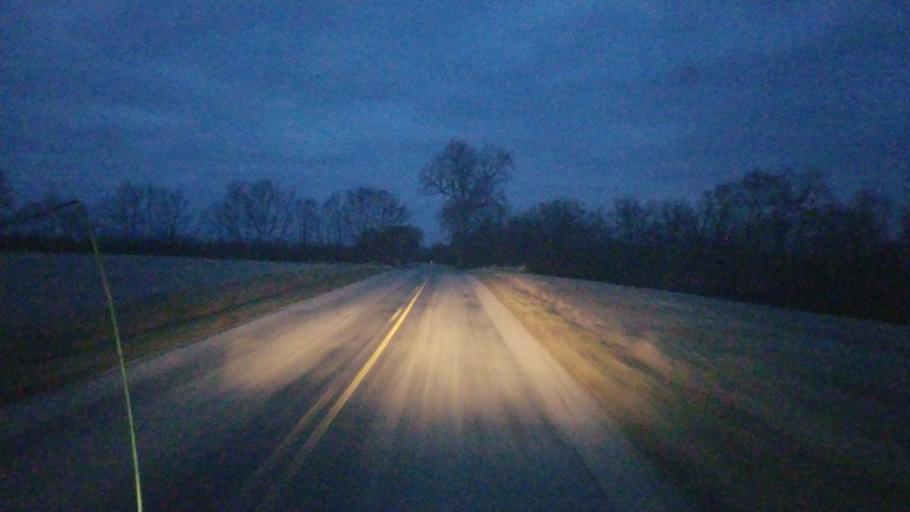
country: US
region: Ohio
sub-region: Marion County
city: Prospect
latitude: 40.4579
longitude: -83.1920
